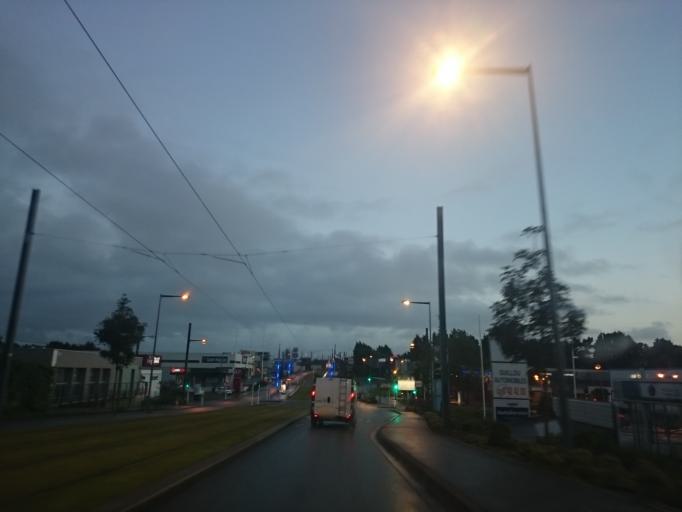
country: FR
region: Brittany
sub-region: Departement du Finistere
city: Gouesnou
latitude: 48.4256
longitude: -4.4672
